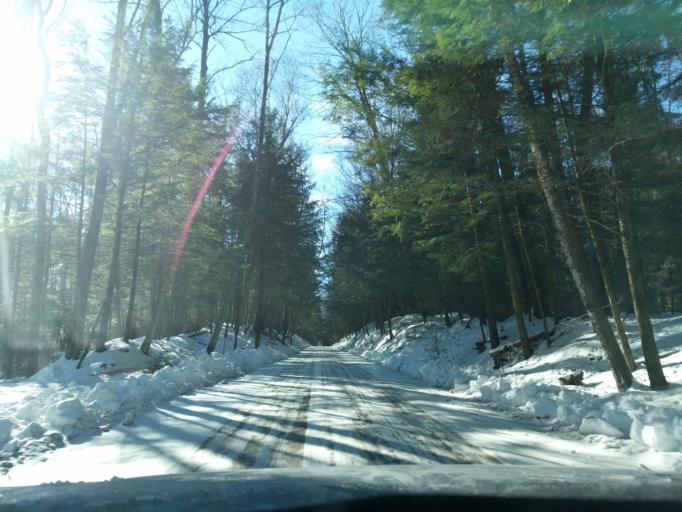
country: US
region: Wisconsin
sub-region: Menominee County
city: Keshena
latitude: 45.0935
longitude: -88.6184
